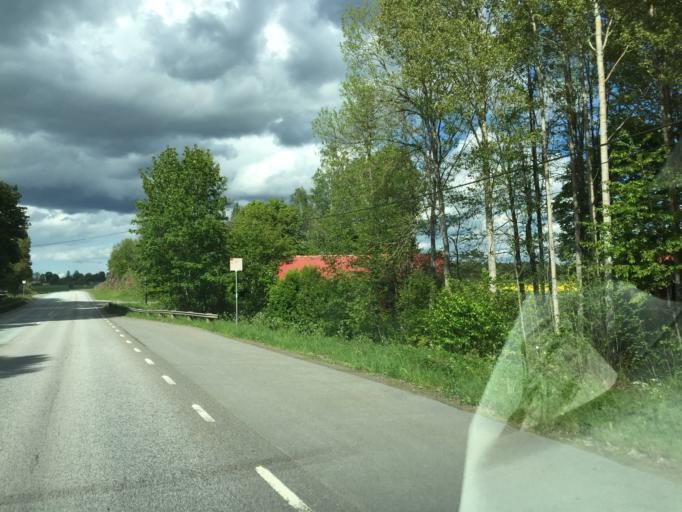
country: SE
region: OEstergoetland
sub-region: Finspangs Kommun
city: Finspang
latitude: 58.6399
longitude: 15.8220
